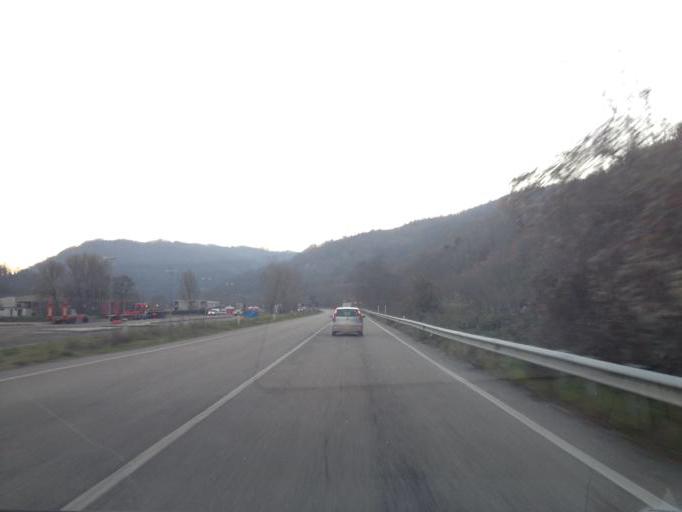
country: IT
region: The Marches
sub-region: Provincia di Ascoli Piceno
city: Arquata del Tronto
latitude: 42.7471
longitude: 13.2696
